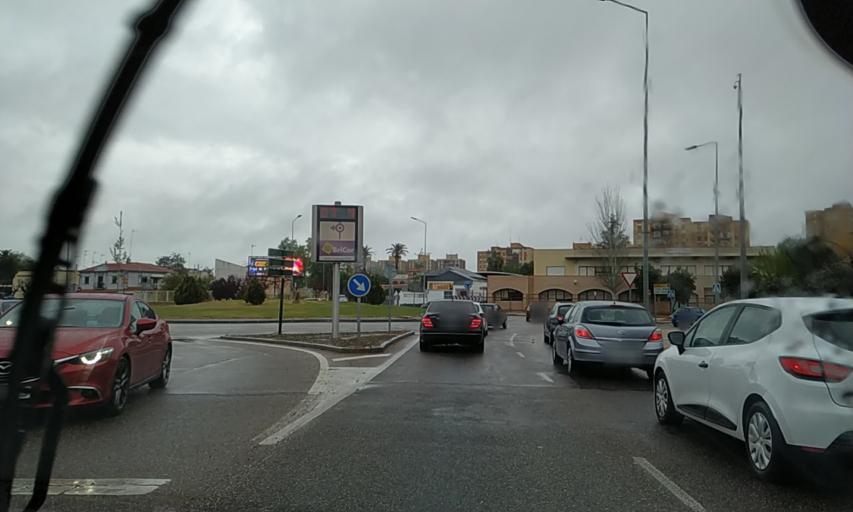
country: ES
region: Extremadura
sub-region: Provincia de Badajoz
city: Badajoz
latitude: 38.8835
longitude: -6.9850
